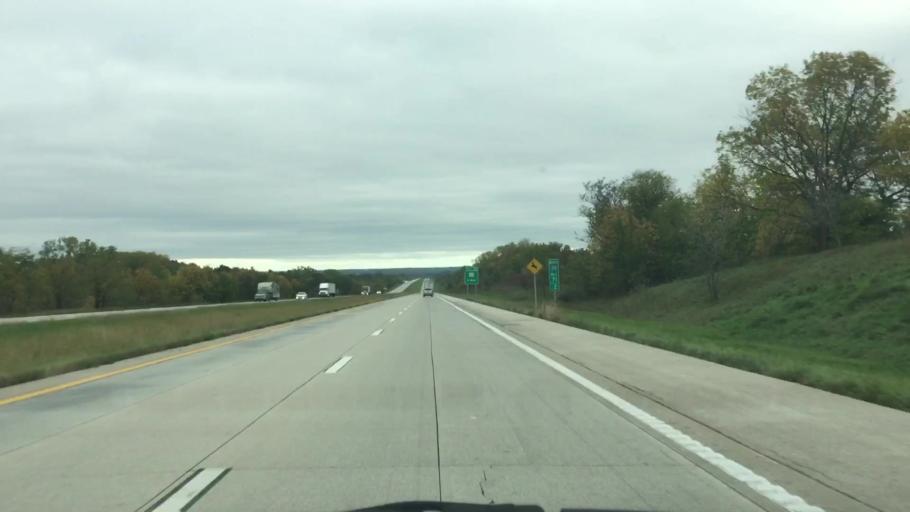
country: US
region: Missouri
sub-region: Daviess County
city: Gallatin
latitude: 39.9773
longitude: -94.0941
